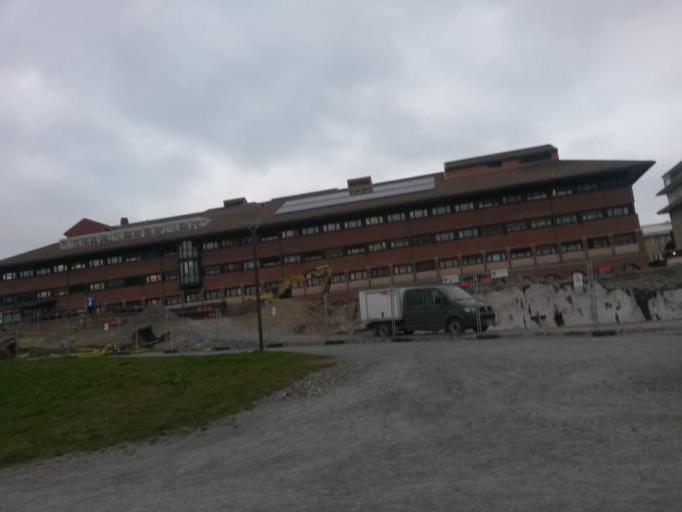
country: SE
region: Vaesterbotten
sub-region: Skelleftea Kommun
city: Skelleftea
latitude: 64.7482
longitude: 20.9538
